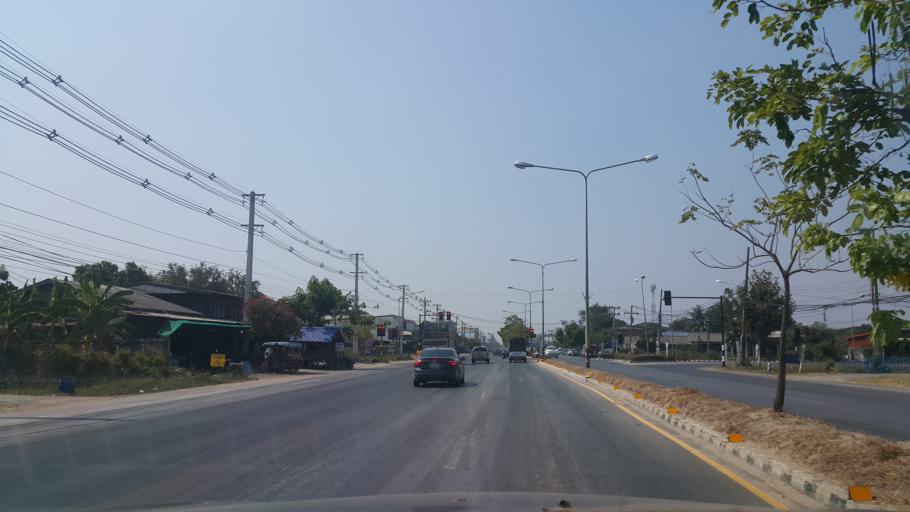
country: TH
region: Nakhon Ratchasima
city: Chum Phuang
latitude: 15.3529
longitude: 102.7520
